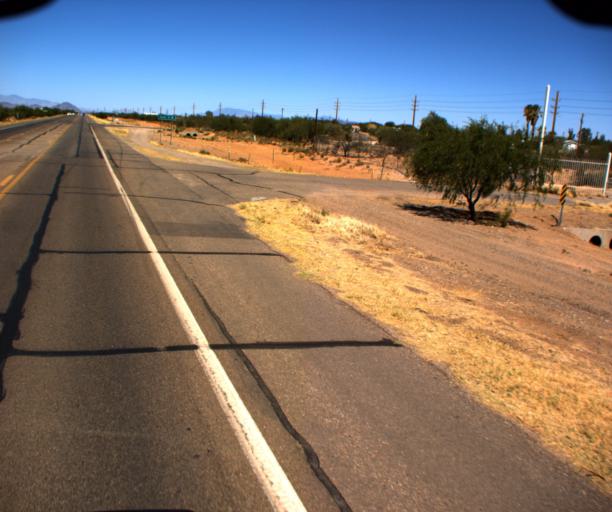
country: US
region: Arizona
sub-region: Pima County
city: Three Points
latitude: 32.0791
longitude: -111.3071
